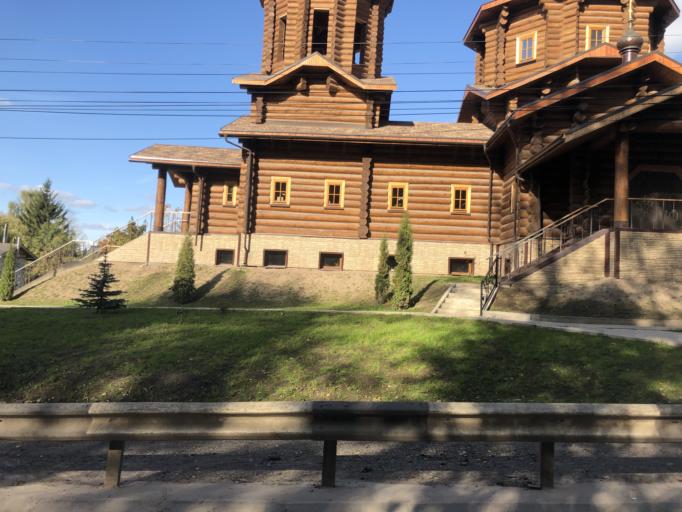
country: RU
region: Tverskaya
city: Rzhev
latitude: 56.2622
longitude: 34.3446
